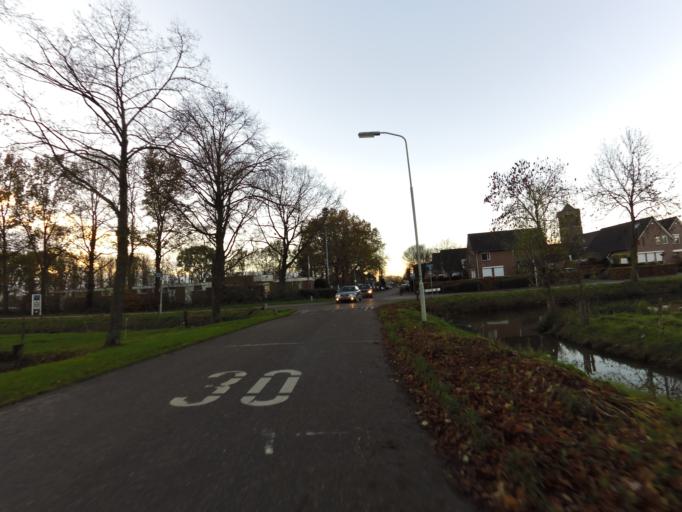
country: NL
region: Gelderland
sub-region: Gemeente Montferland
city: s-Heerenberg
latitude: 51.8848
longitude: 6.3066
